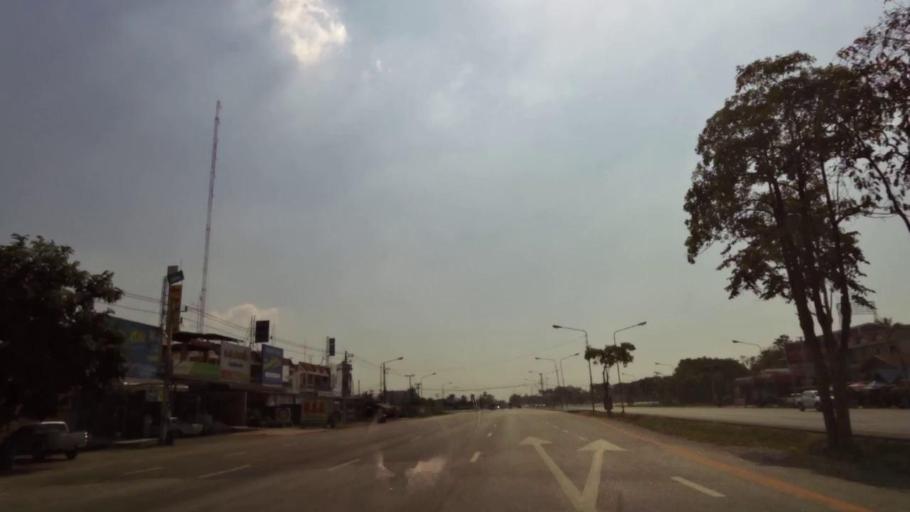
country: TH
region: Phichit
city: Bueng Na Rang
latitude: 16.1260
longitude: 100.1256
